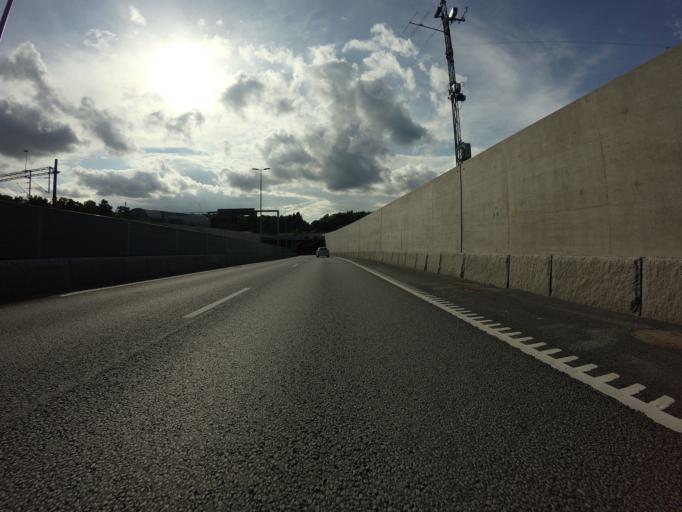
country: SE
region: Stockholm
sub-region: Stockholms Kommun
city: OEstermalm
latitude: 59.3520
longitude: 18.0908
